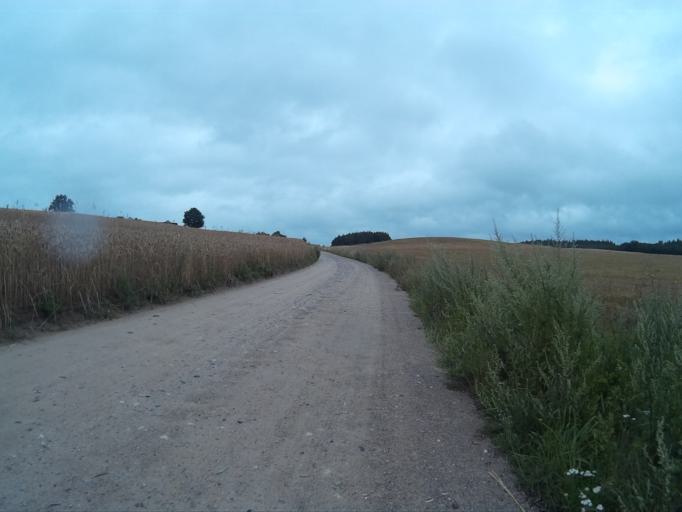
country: PL
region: Kujawsko-Pomorskie
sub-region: Powiat tucholski
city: Tuchola
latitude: 53.5602
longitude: 17.8448
